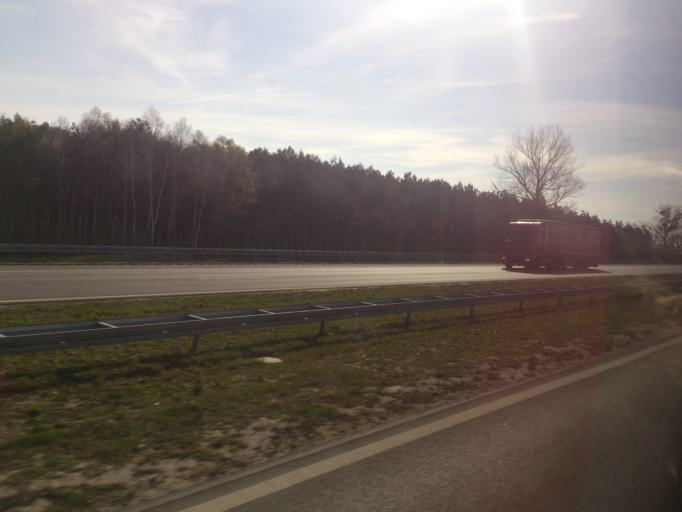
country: PL
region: Kujawsko-Pomorskie
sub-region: Powiat aleksandrowski
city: Ciechocinek
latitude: 52.8531
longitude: 18.7775
